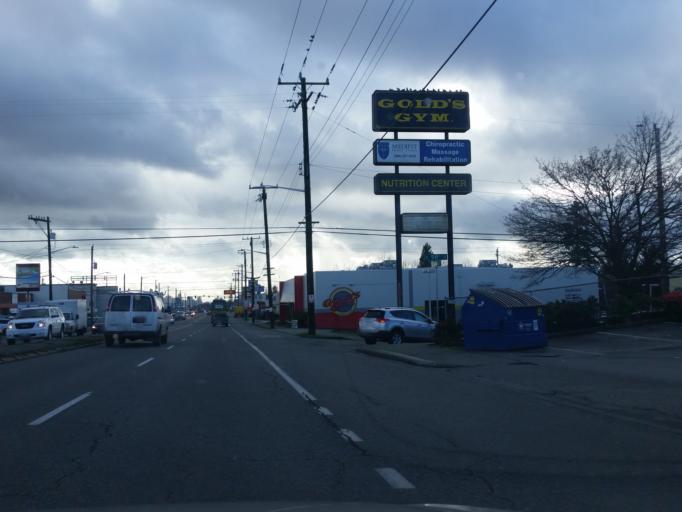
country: US
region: Washington
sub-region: King County
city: Shoreline
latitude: 47.7008
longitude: -122.3447
